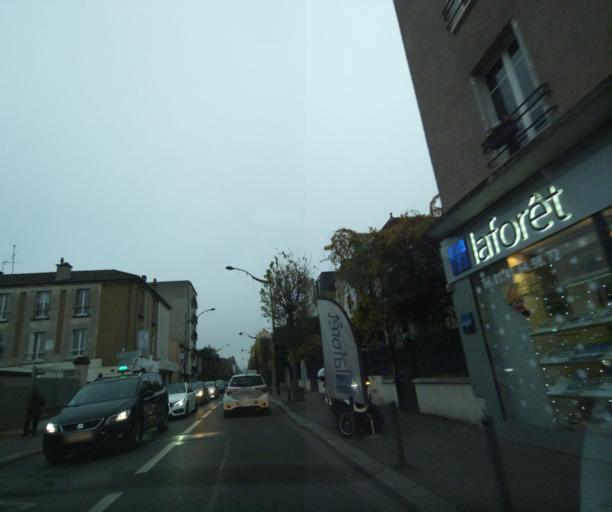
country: FR
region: Ile-de-France
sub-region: Departement de Seine-Saint-Denis
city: Les Pavillons-sous-Bois
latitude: 48.9042
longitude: 2.5050
